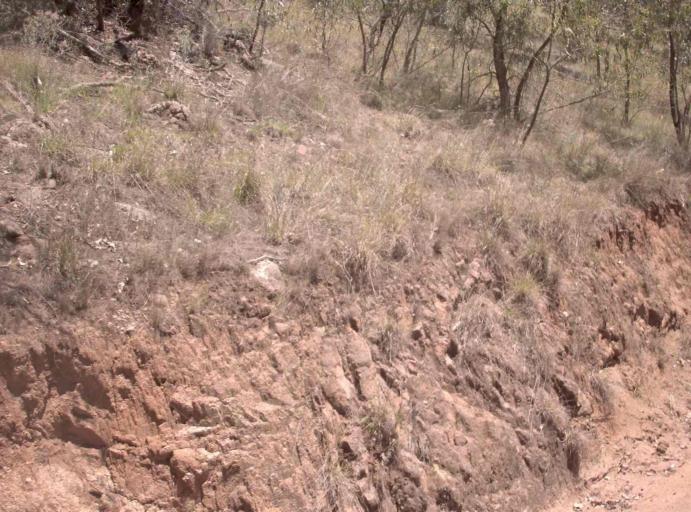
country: AU
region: New South Wales
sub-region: Snowy River
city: Jindabyne
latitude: -36.9324
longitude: 148.3555
